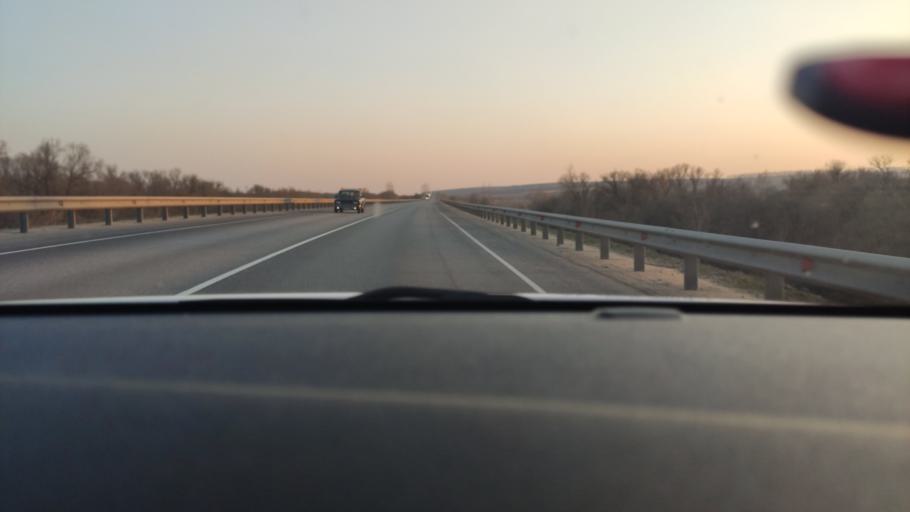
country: RU
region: Voronezj
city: Kolodeznyy
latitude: 51.3444
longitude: 39.1727
